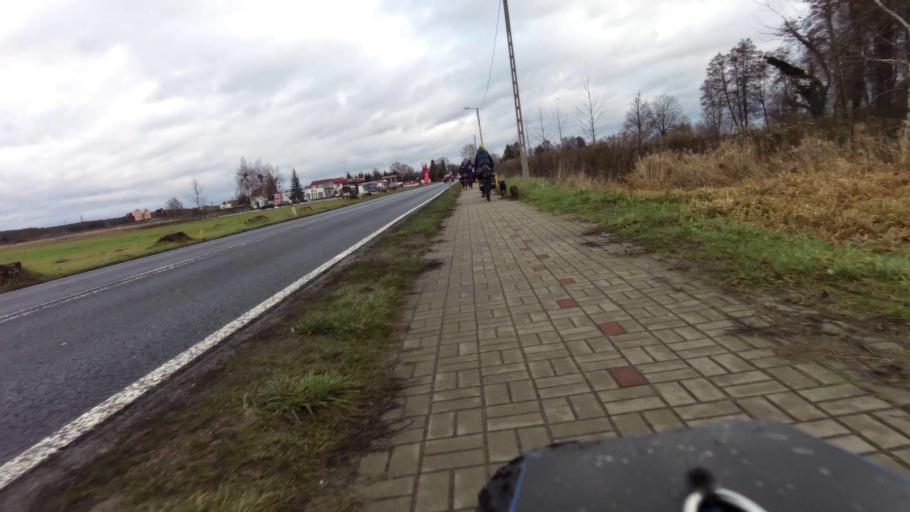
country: PL
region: Lubusz
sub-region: Powiat gorzowski
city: Witnica
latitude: 52.6747
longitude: 14.9155
